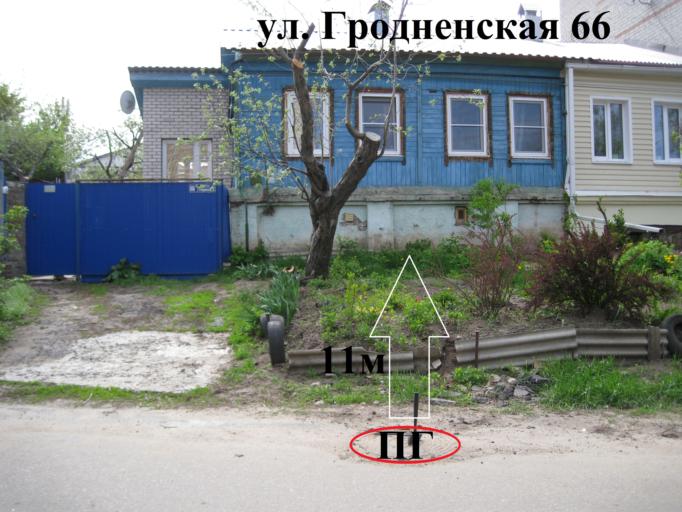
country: RU
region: Voronezj
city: Voronezh
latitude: 51.6479
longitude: 39.1876
